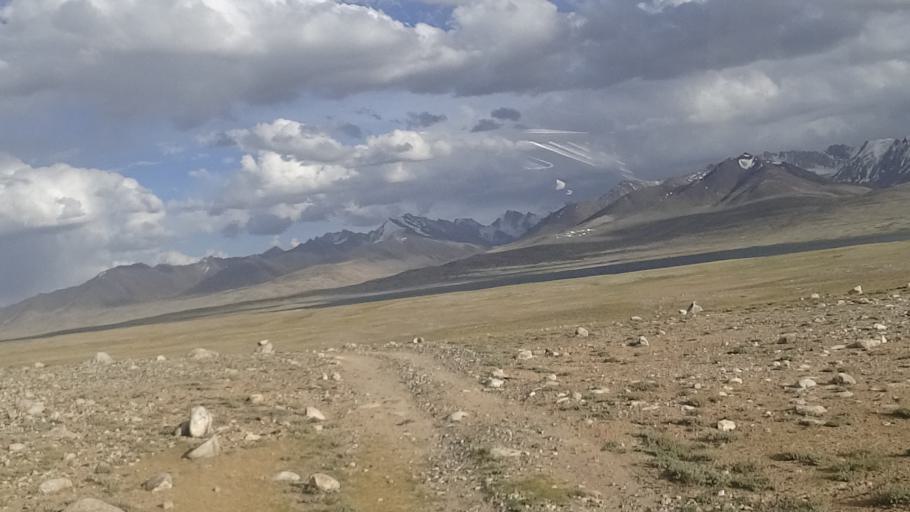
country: TJ
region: Gorno-Badakhshan
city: Murghob
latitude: 37.4626
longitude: 73.6150
